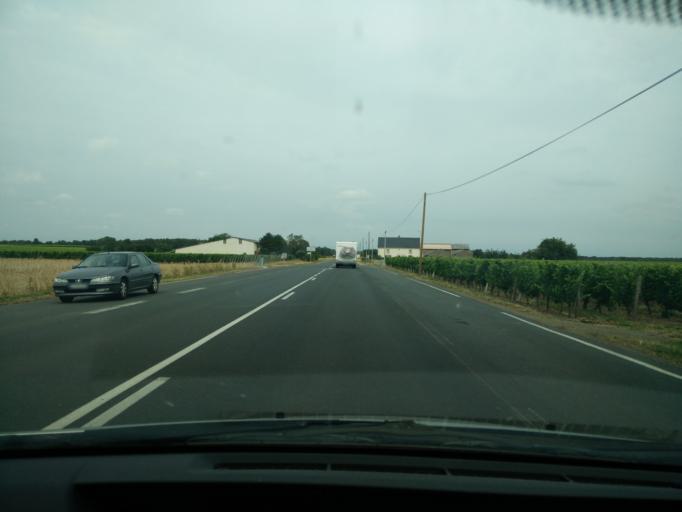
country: FR
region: Pays de la Loire
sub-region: Departement de Maine-et-Loire
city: Montreuil-Bellay
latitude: 47.1431
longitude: -0.1635
